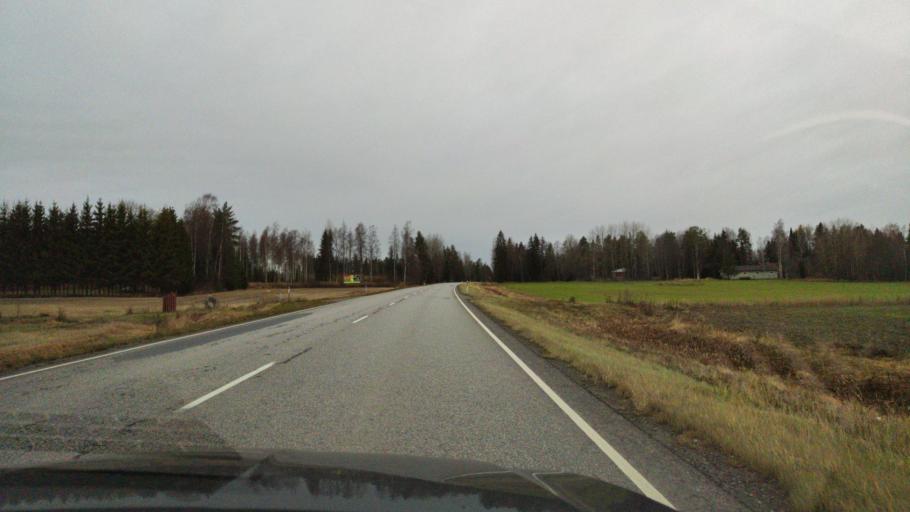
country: FI
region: Varsinais-Suomi
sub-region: Loimaa
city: Ylaene
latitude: 60.8605
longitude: 22.4161
